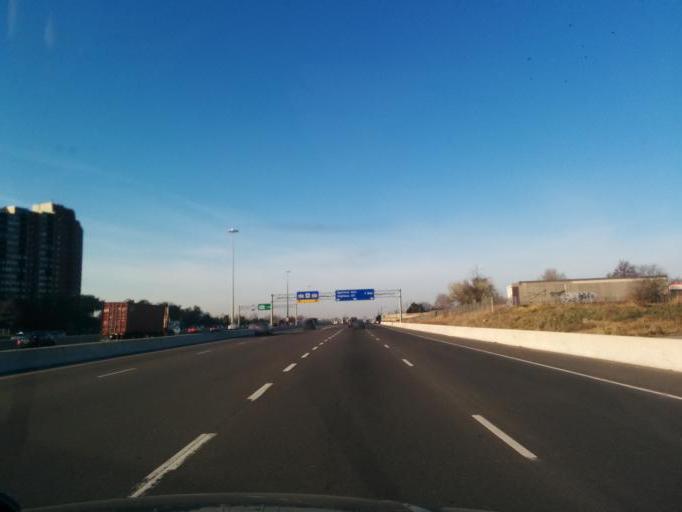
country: CA
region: Ontario
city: Etobicoke
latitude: 43.6547
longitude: -79.5673
